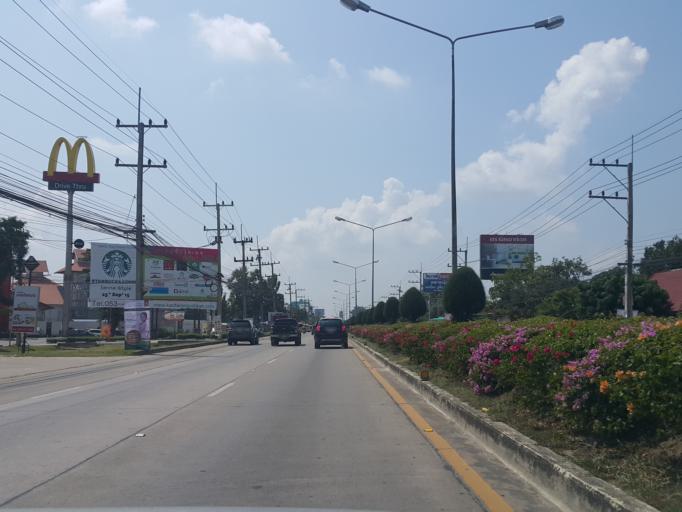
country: TH
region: Chiang Mai
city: Hang Dong
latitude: 18.7017
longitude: 98.9312
